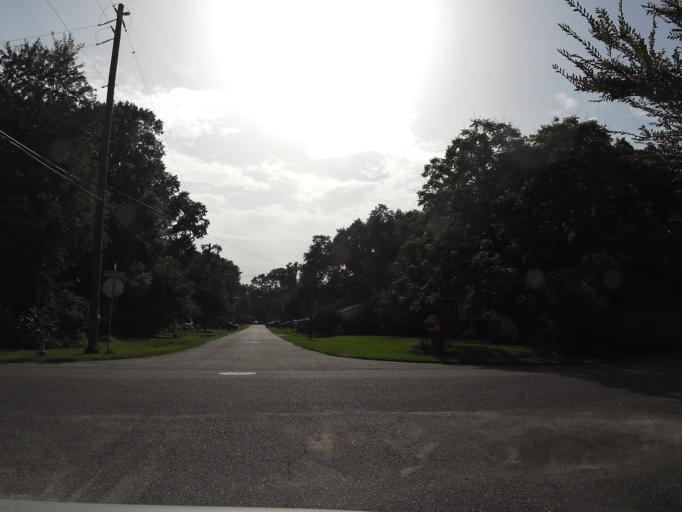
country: US
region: Florida
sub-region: Duval County
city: Jacksonville
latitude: 30.3039
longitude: -81.7242
